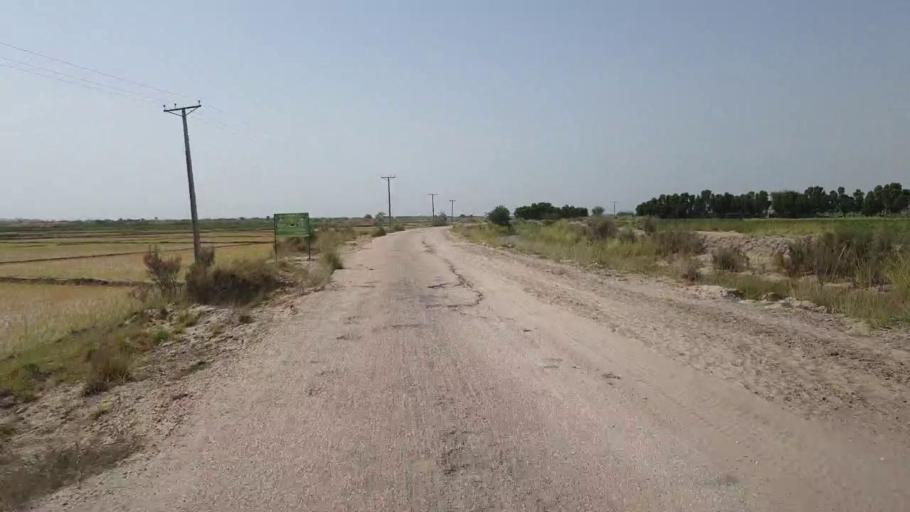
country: PK
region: Sindh
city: Jam Sahib
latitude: 26.4186
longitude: 68.9079
